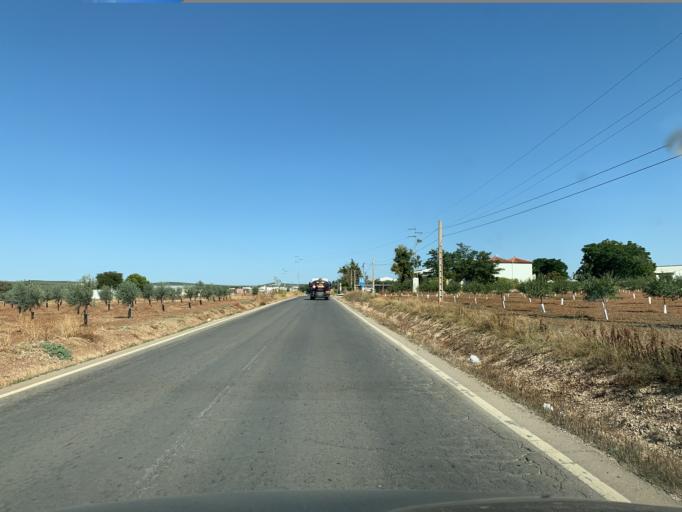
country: ES
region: Andalusia
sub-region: Provincia de Sevilla
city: El Rubio
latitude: 37.3630
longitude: -4.9753
